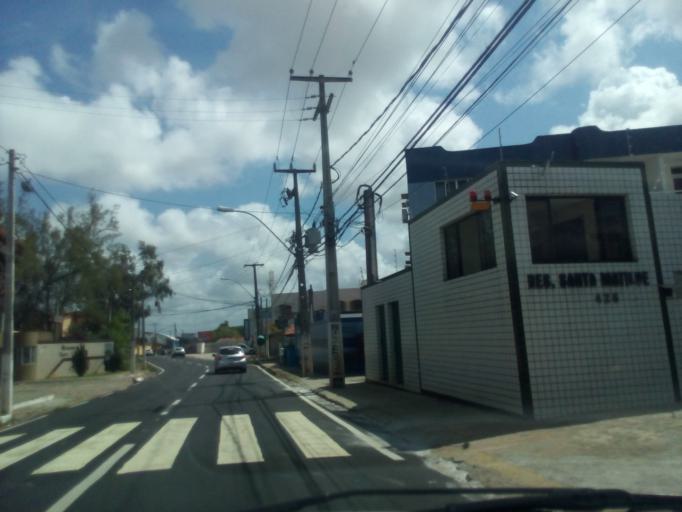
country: BR
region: Rio Grande do Norte
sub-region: Natal
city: Natal
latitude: -5.8539
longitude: -35.2060
